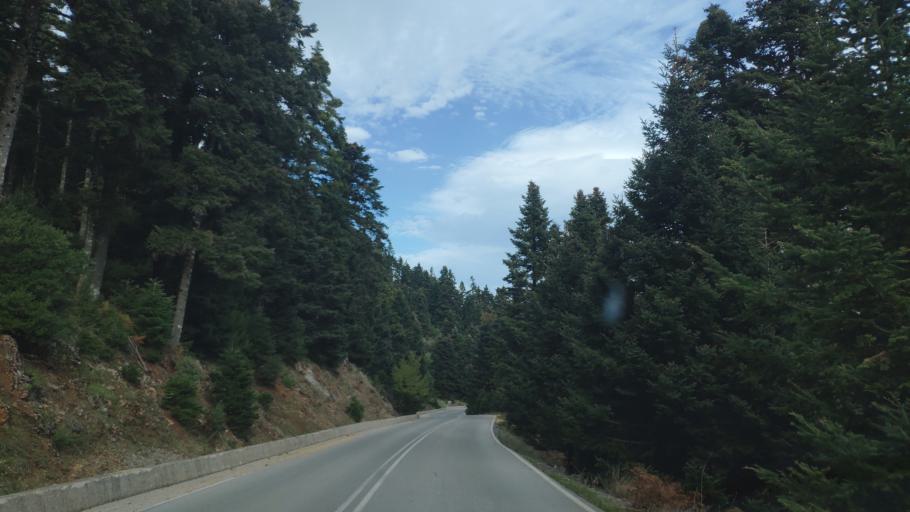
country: GR
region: Central Greece
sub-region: Nomos Fokidos
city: Amfissa
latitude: 38.6593
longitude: 22.3813
